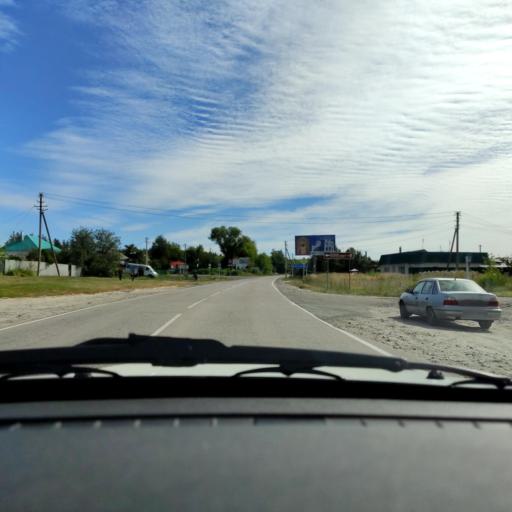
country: RU
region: Voronezj
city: Uglyanets
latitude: 51.8588
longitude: 39.6717
